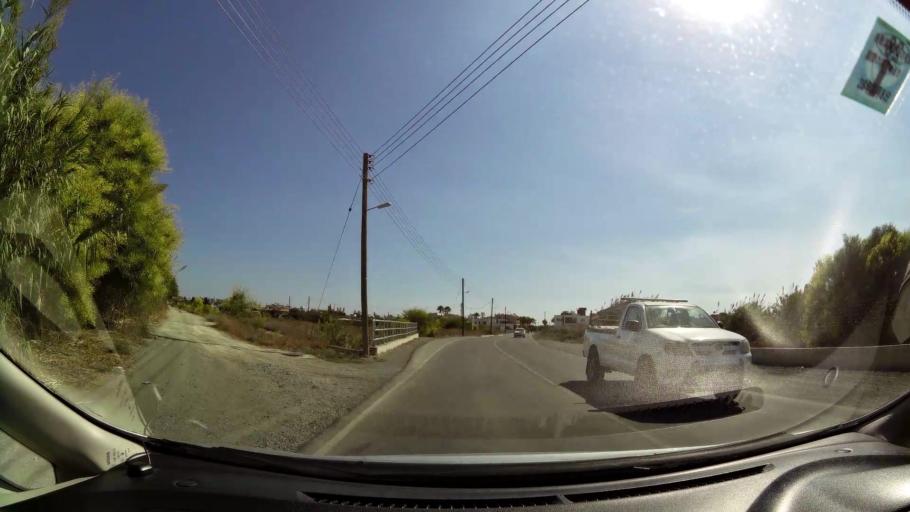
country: CY
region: Larnaka
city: Livadia
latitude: 34.9526
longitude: 33.6215
